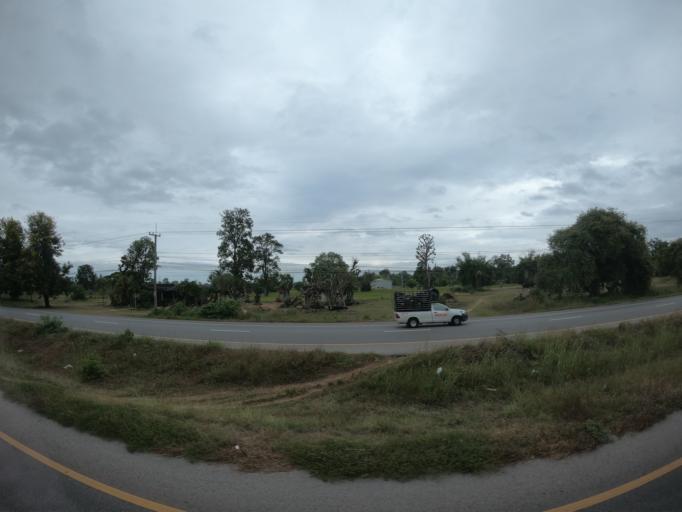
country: TH
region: Roi Et
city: Changhan
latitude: 16.0974
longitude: 103.5339
